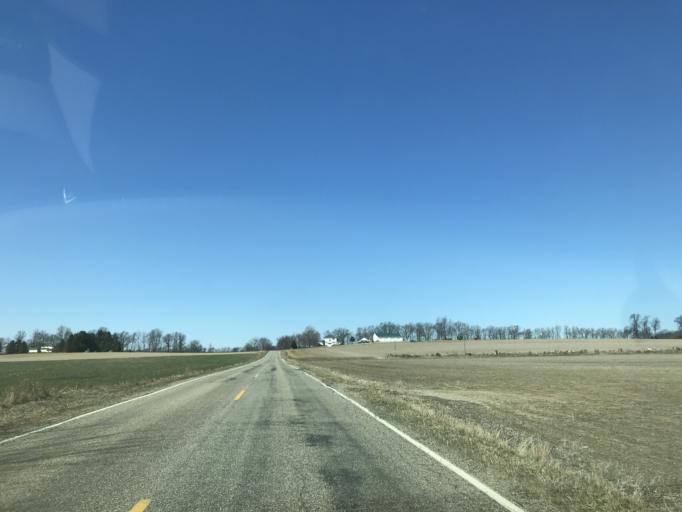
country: US
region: Michigan
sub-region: Hillsdale County
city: Jonesville
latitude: 41.9855
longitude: -84.7220
